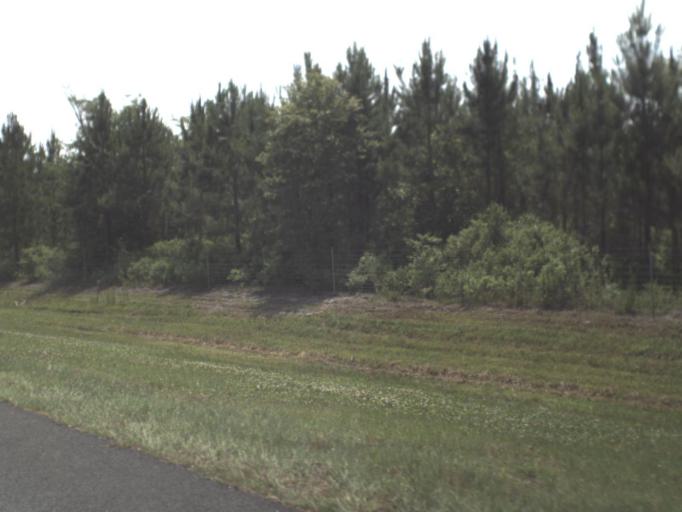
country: US
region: Florida
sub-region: Nassau County
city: Callahan
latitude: 30.6016
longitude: -81.7558
